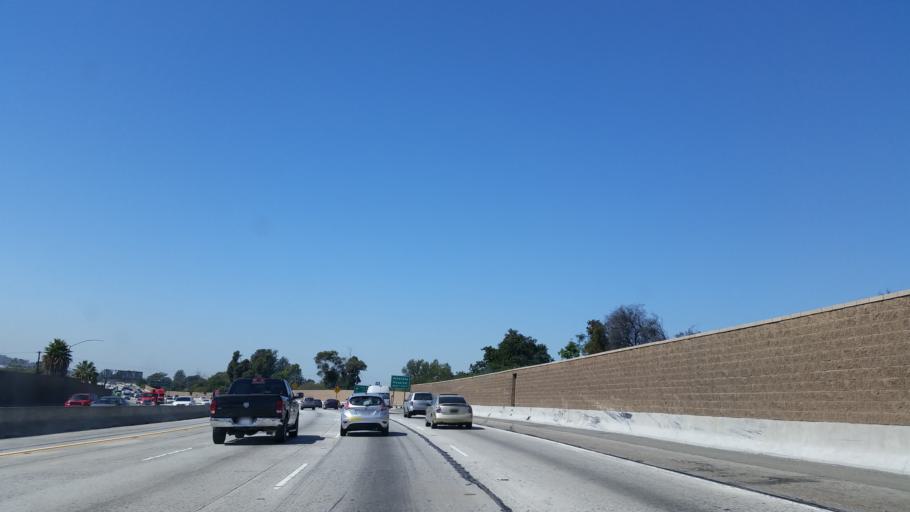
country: US
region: California
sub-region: Orange County
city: Rossmoor
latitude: 33.8023
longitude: -118.1153
